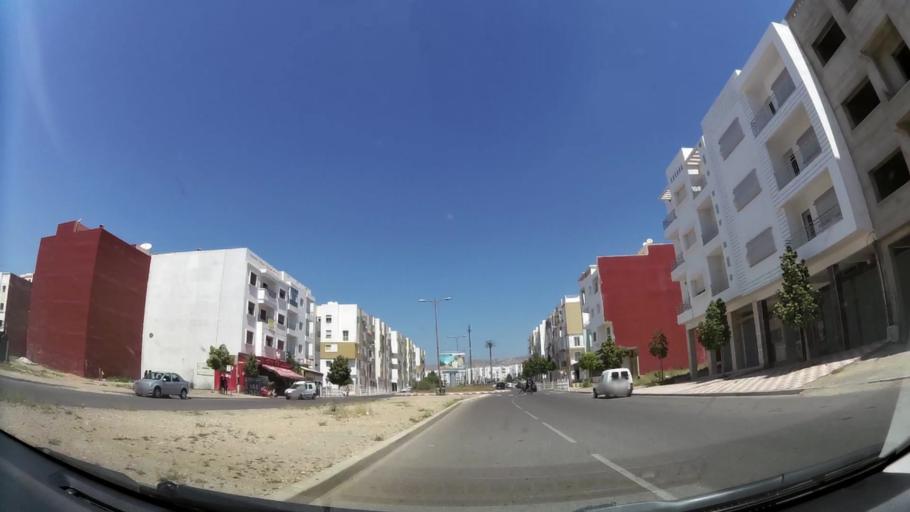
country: MA
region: Oued ed Dahab-Lagouira
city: Dakhla
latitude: 30.4317
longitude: -9.5563
